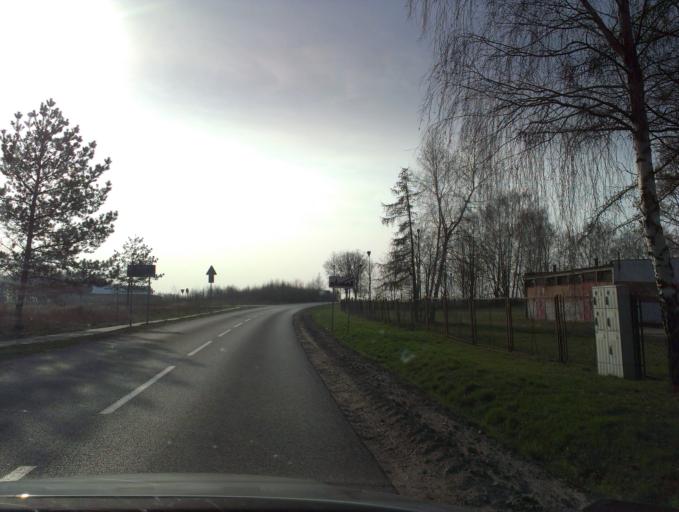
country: PL
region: Kujawsko-Pomorskie
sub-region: Powiat sepolenski
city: Sepolno Krajenskie
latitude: 53.4490
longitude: 17.5140
